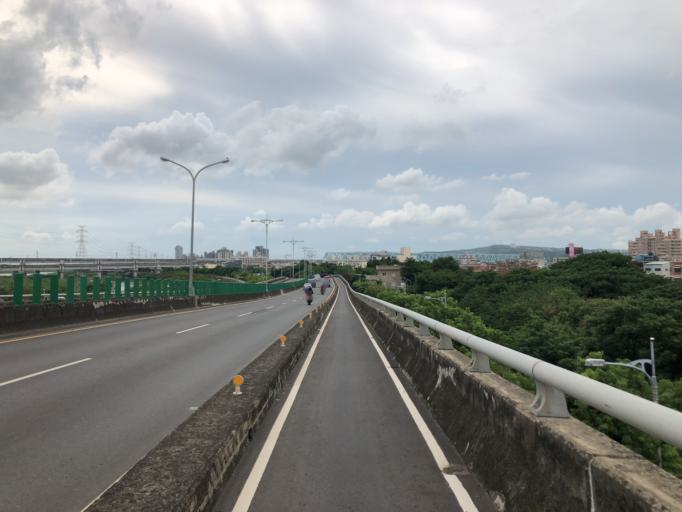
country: TW
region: Taiwan
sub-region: Changhua
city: Chang-hua
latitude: 24.1008
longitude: 120.6233
